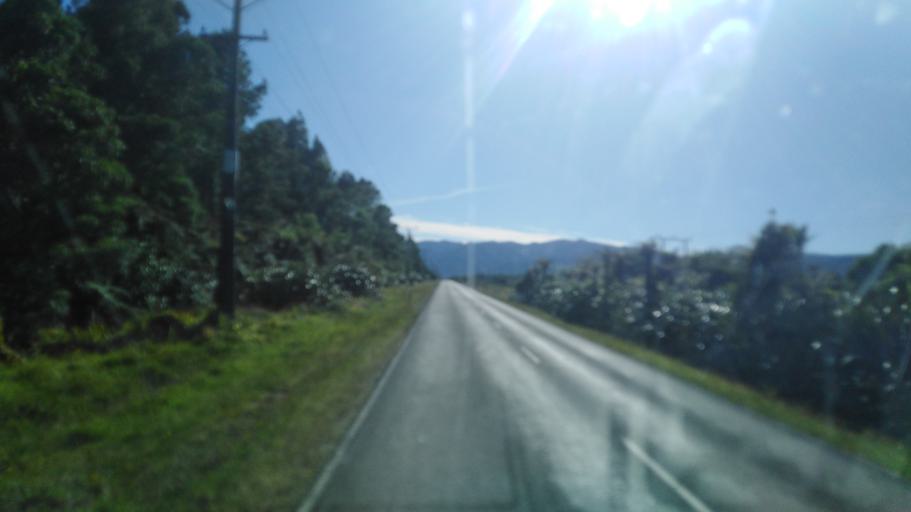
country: NZ
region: West Coast
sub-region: Buller District
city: Westport
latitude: -41.7421
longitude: 171.6932
